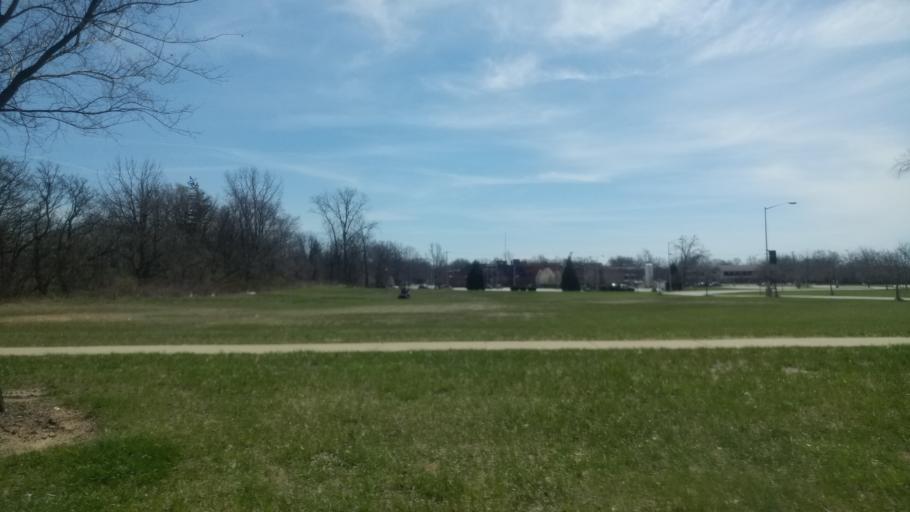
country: US
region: Ohio
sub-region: Wood County
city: Bowling Green
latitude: 41.3789
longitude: -83.6657
